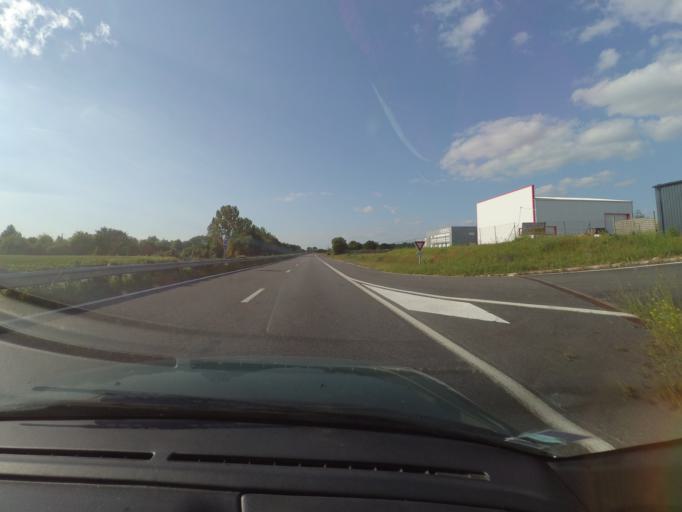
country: FR
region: Pays de la Loire
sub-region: Departement de la Vendee
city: Saligny
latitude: 46.8012
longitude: -1.4315
